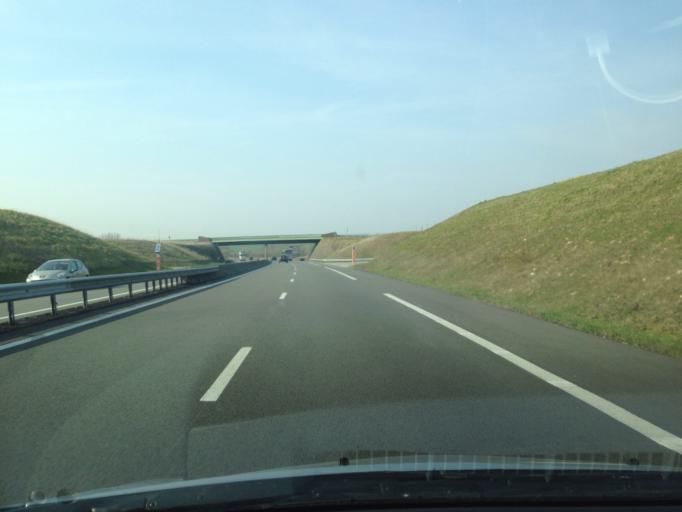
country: FR
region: Picardie
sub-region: Departement de la Somme
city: Rue
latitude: 50.3189
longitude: 1.7208
